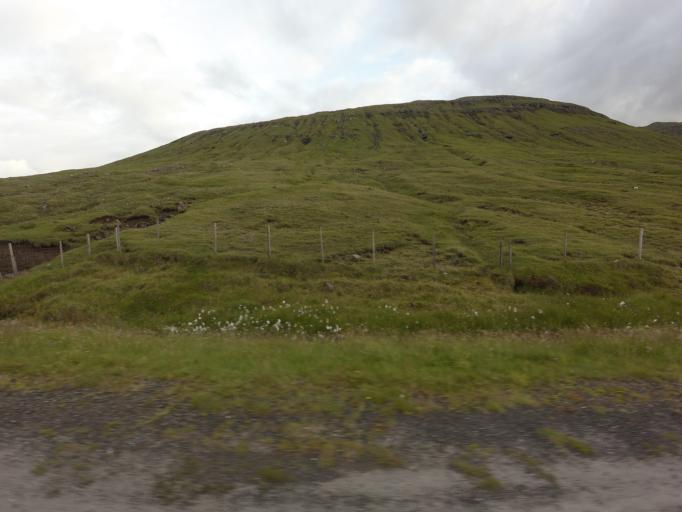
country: FO
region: Streymoy
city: Kollafjordhur
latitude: 62.1803
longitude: -6.9923
